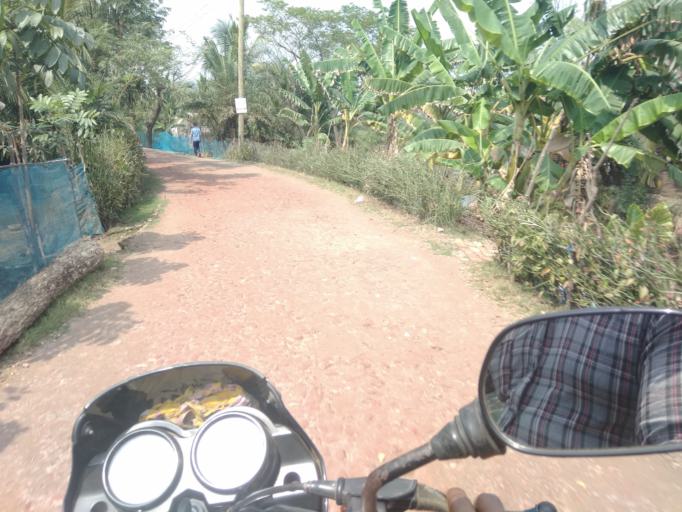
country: IN
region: West Bengal
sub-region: North 24 Parganas
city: Taki
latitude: 22.3024
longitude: 89.2680
